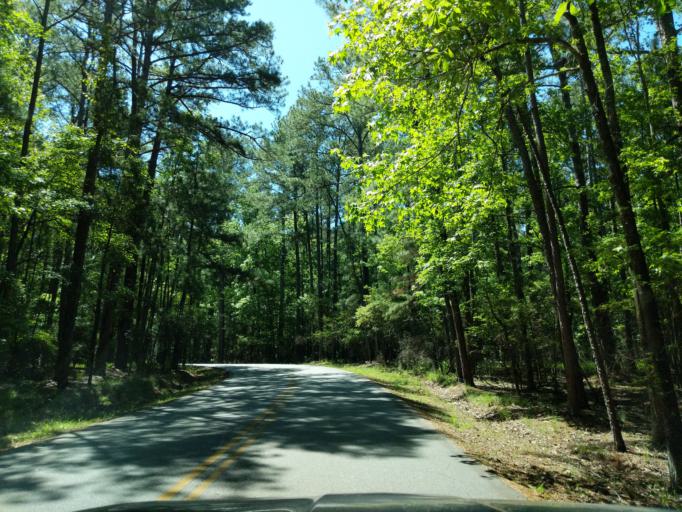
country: US
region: Georgia
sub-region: Columbia County
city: Appling
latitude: 33.6644
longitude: -82.3844
